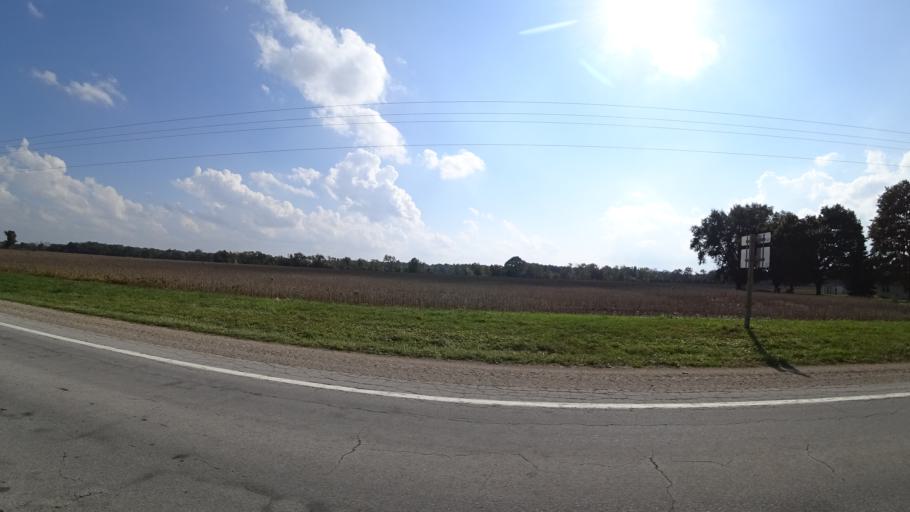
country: US
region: Michigan
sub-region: Saint Joseph County
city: Colon
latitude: 42.0102
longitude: -85.3804
